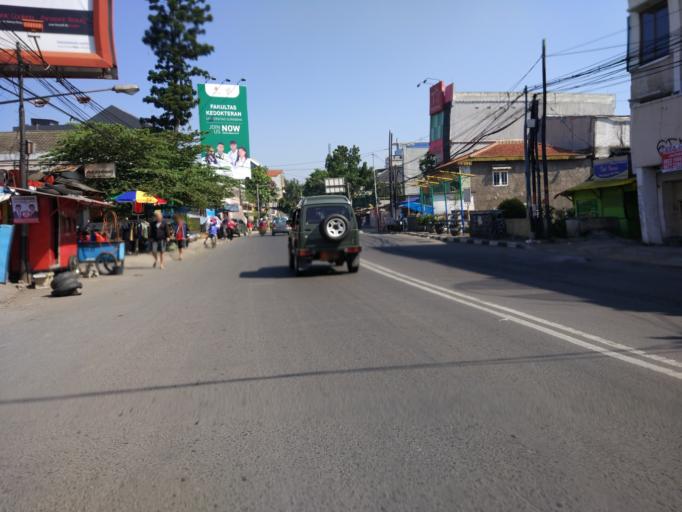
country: ID
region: West Java
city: Bandung
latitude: -6.9309
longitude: 107.6407
